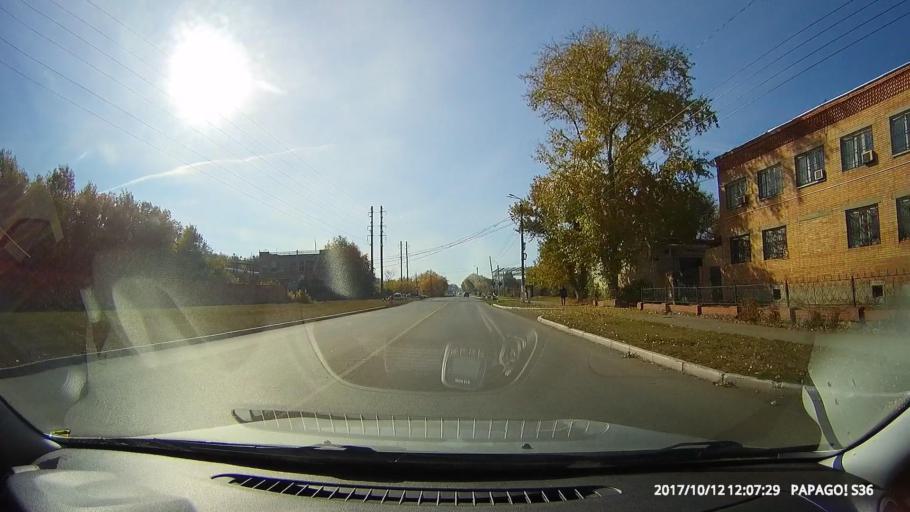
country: RU
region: Samara
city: Chapayevsk
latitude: 52.9668
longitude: 49.7010
